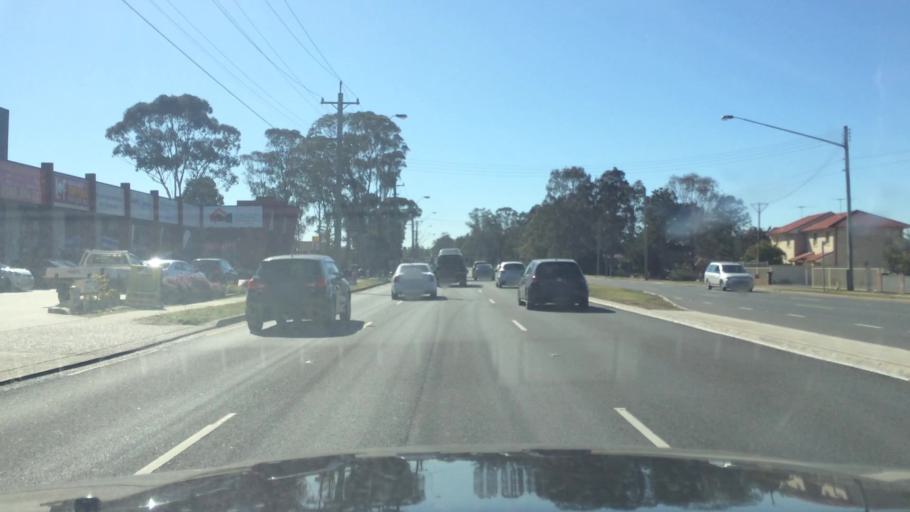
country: AU
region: New South Wales
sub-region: Campbelltown Municipality
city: Glenfield
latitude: -33.9543
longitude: 150.8975
